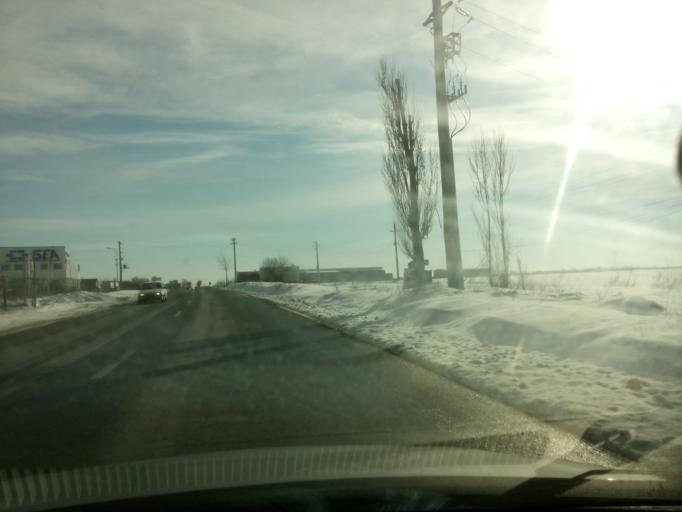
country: RO
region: Ilfov
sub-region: Comuna Popesti-Leordeni
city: Popesti-Leordeni
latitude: 44.3671
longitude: 26.1871
